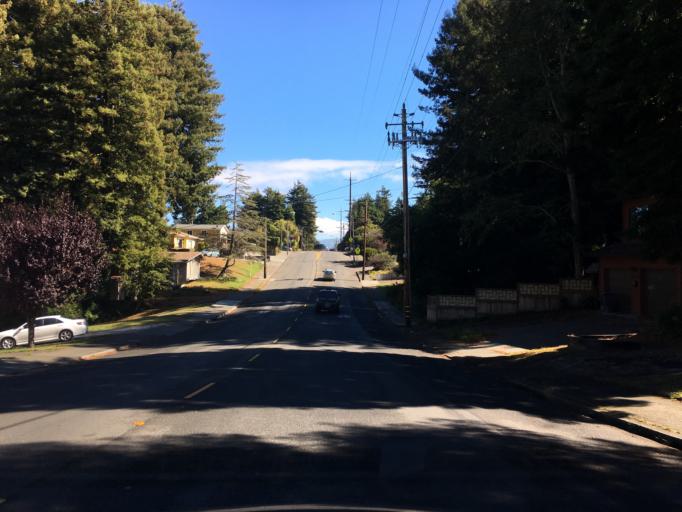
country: US
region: California
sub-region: Humboldt County
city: Cutten
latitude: 40.7805
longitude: -124.1439
